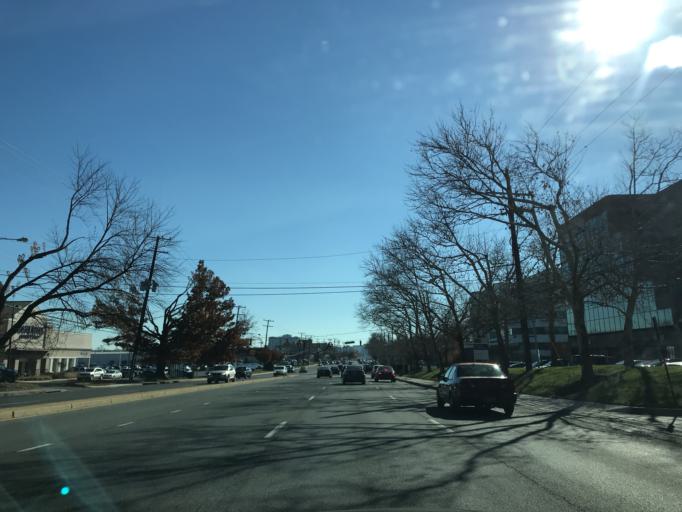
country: US
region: Maryland
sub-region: Montgomery County
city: North Bethesda
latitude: 39.0678
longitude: -77.1291
